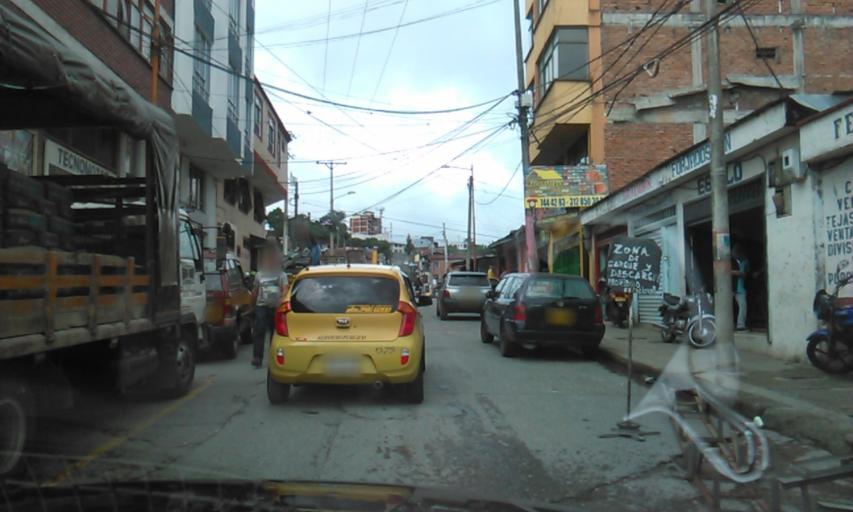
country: CO
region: Quindio
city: Armenia
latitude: 4.5377
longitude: -75.6745
